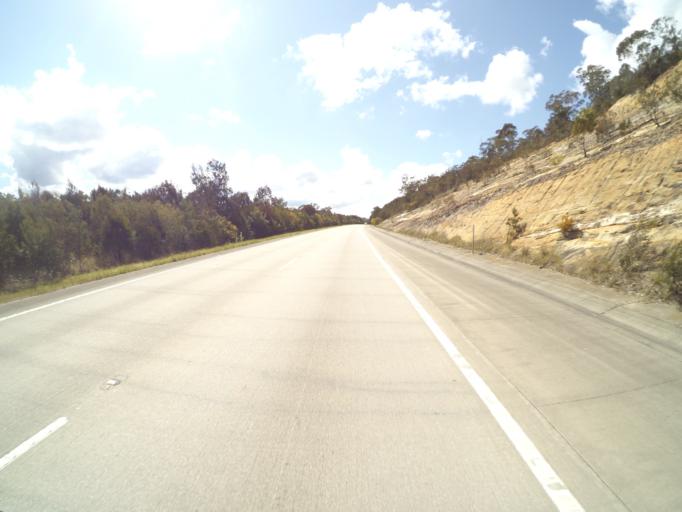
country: AU
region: New South Wales
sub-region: Wingecarribee
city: Colo Vale
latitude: -34.4252
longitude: 150.4706
